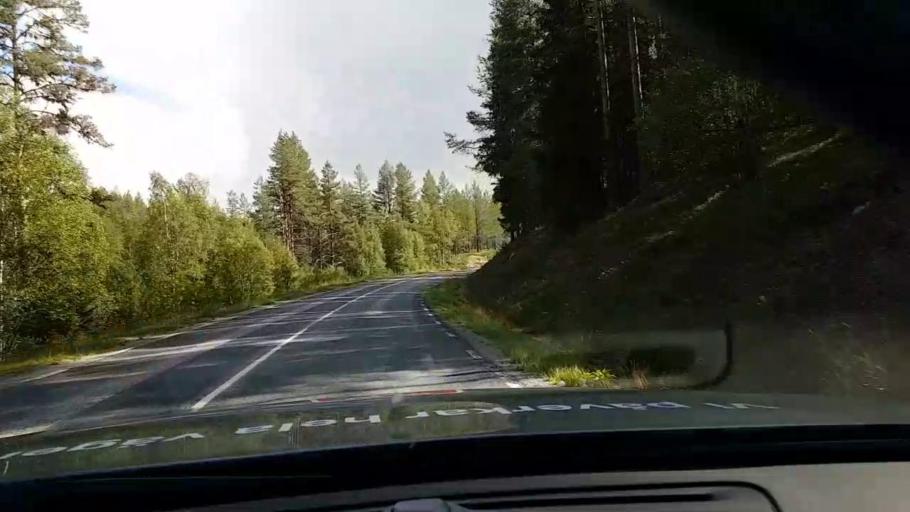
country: SE
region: Vaesterbotten
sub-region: Asele Kommun
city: Asele
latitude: 63.8583
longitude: 17.3834
